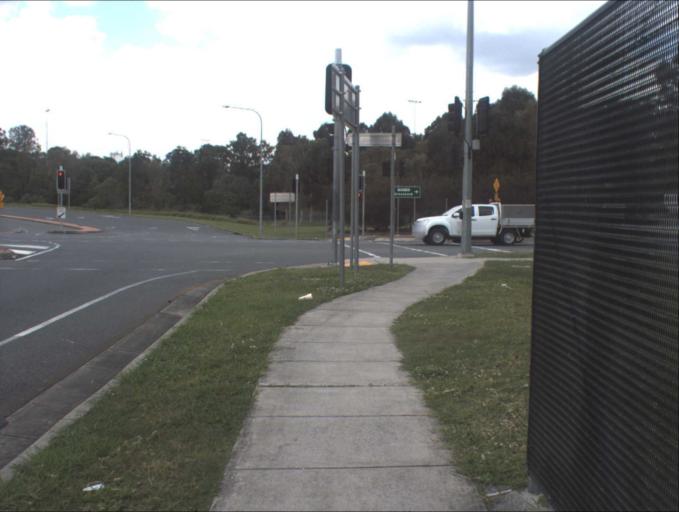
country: AU
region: Queensland
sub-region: Logan
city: Park Ridge South
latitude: -27.6987
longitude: 153.0363
